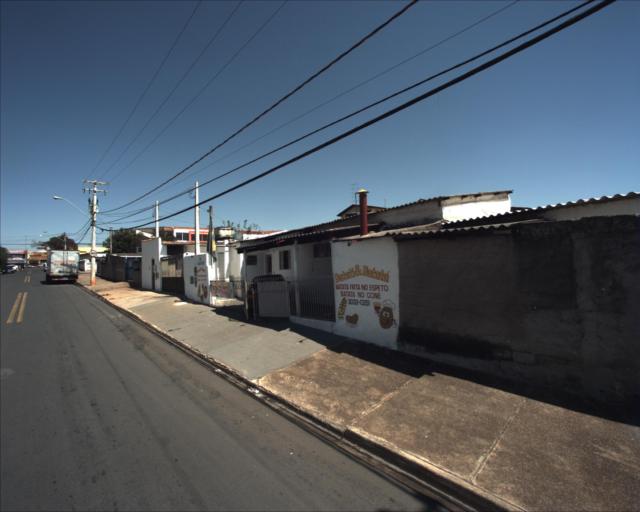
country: BR
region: Sao Paulo
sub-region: Sorocaba
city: Sorocaba
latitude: -23.4756
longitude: -47.4845
